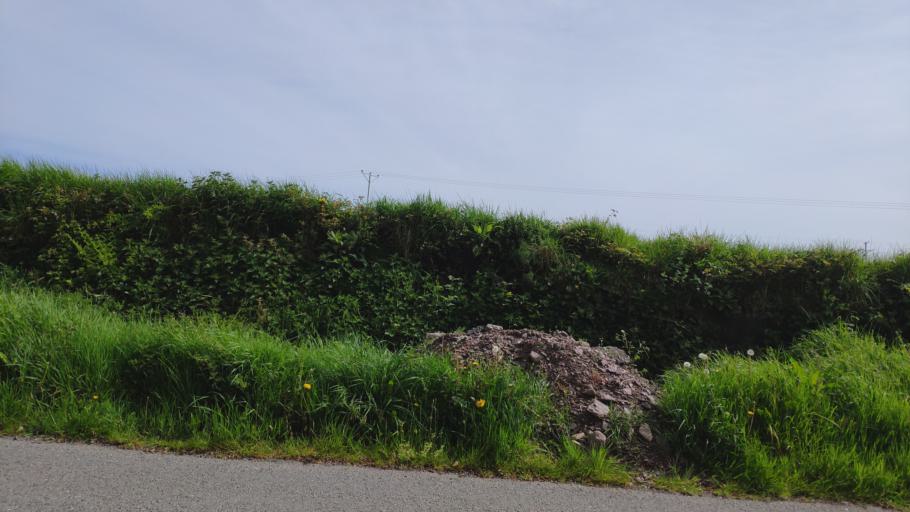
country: IE
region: Munster
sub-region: County Cork
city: Blarney
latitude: 51.9548
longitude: -8.5066
